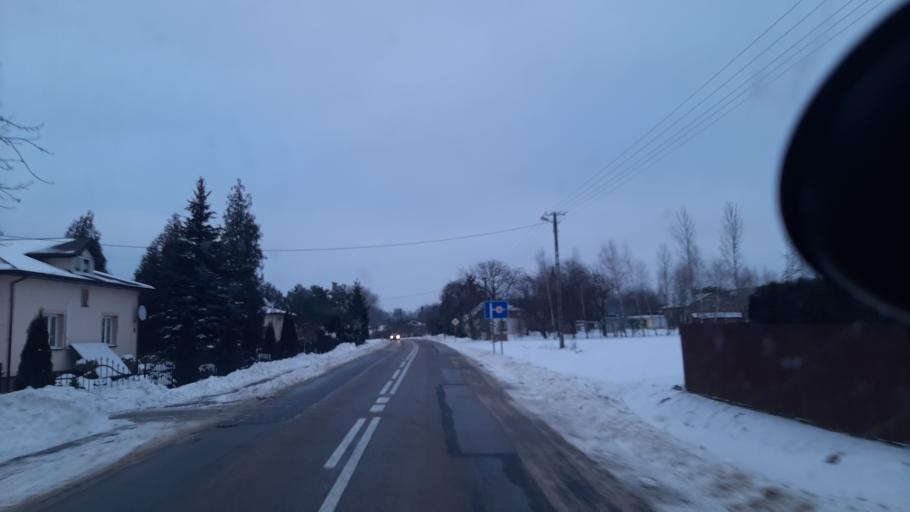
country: PL
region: Lublin Voivodeship
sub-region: Powiat lubelski
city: Jastkow
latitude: 51.3438
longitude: 22.4040
